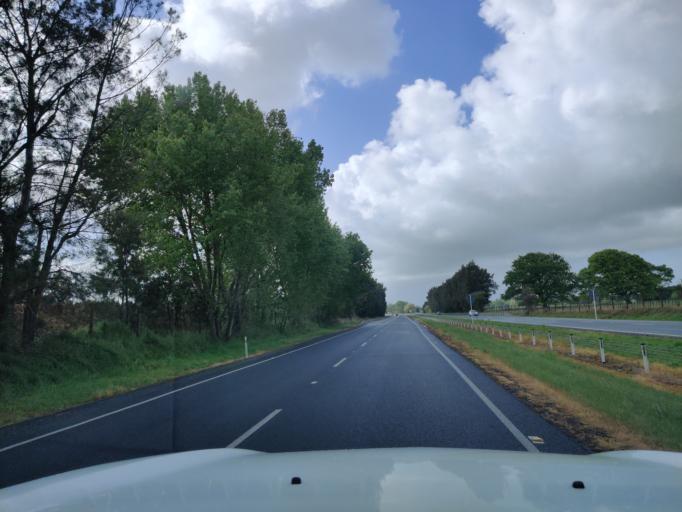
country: NZ
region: Waikato
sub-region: Waipa District
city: Cambridge
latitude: -37.8354
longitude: 175.3646
